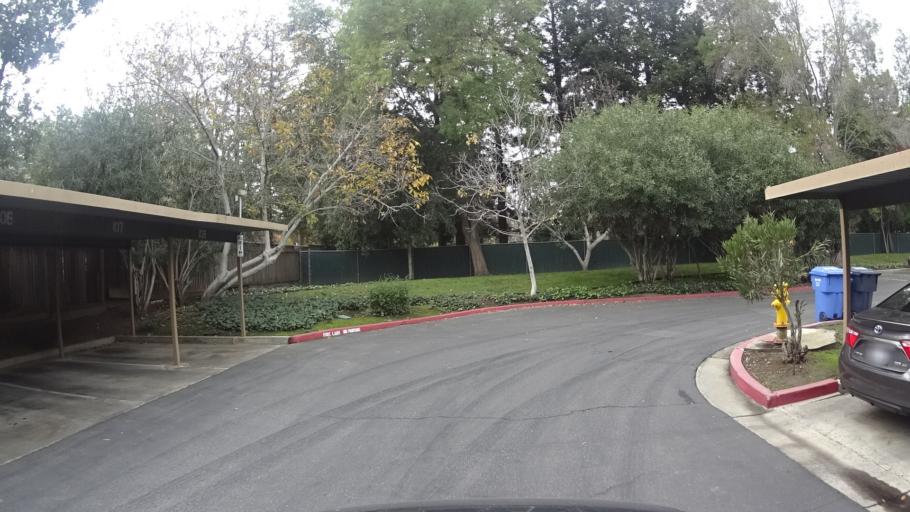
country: US
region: California
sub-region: Santa Clara County
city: Sunnyvale
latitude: 37.3646
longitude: -122.0365
